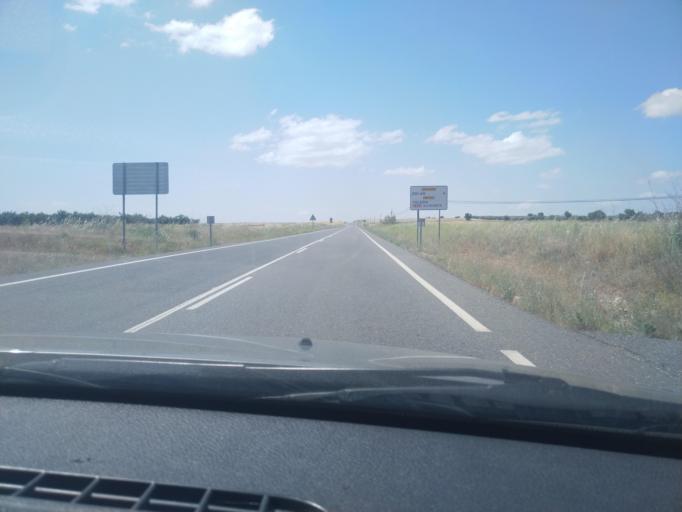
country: ES
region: Castille-La Mancha
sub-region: Province of Toledo
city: Casasbuenas
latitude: 39.7606
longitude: -4.1318
